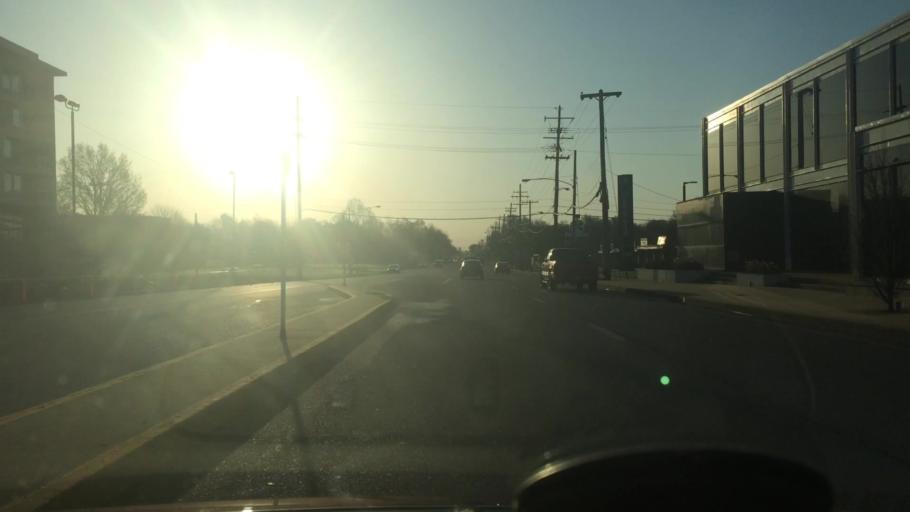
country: US
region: Missouri
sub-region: Greene County
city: Springfield
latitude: 37.1815
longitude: -93.2611
